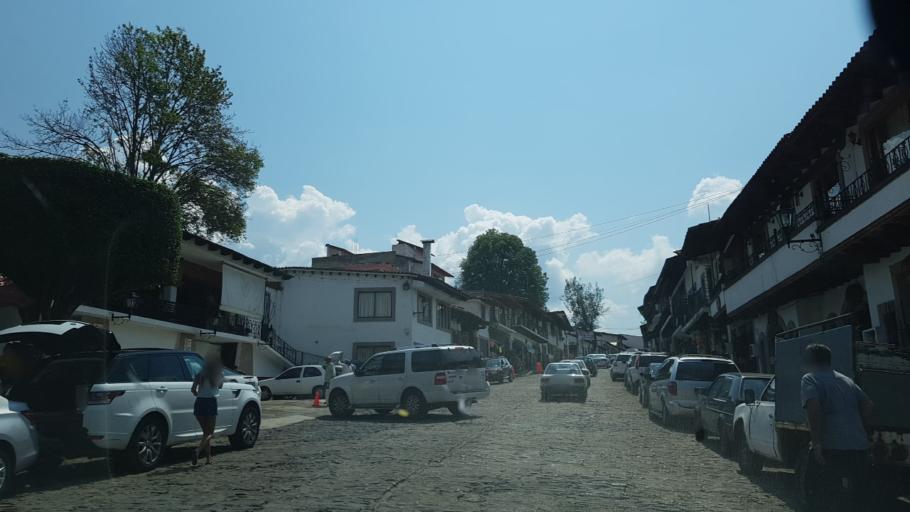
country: MX
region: Mexico
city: Valle de Bravo
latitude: 19.1985
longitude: -100.1317
